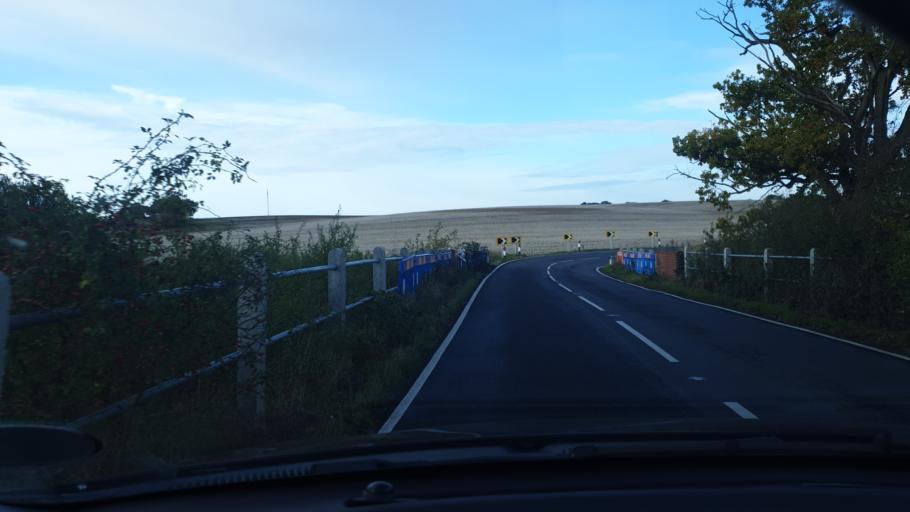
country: GB
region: England
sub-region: Essex
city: Mistley
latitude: 51.9389
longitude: 1.1090
